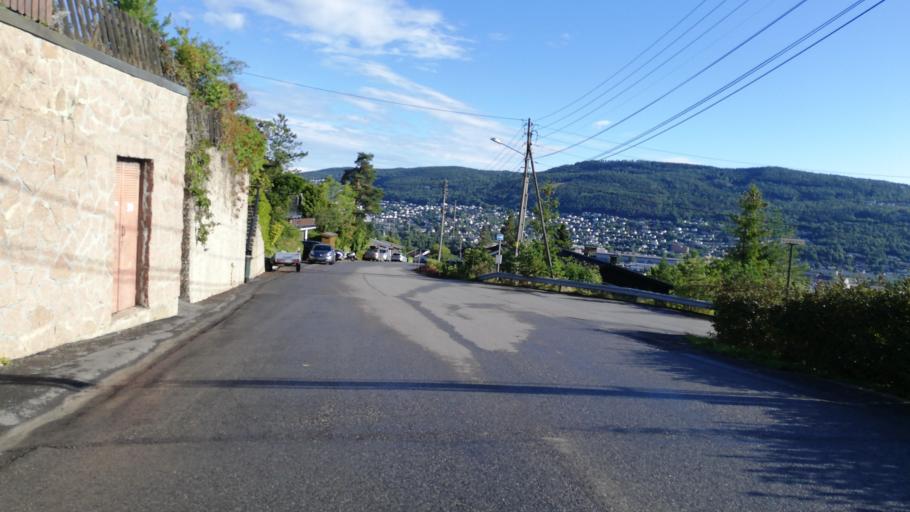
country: NO
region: Buskerud
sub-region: Drammen
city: Drammen
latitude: 59.7562
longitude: 10.1771
